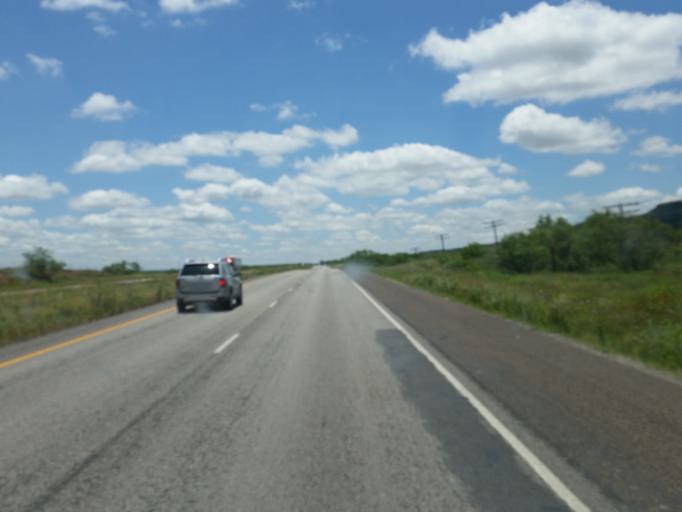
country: US
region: Texas
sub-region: Scurry County
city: Snyder
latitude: 32.9700
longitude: -101.0983
